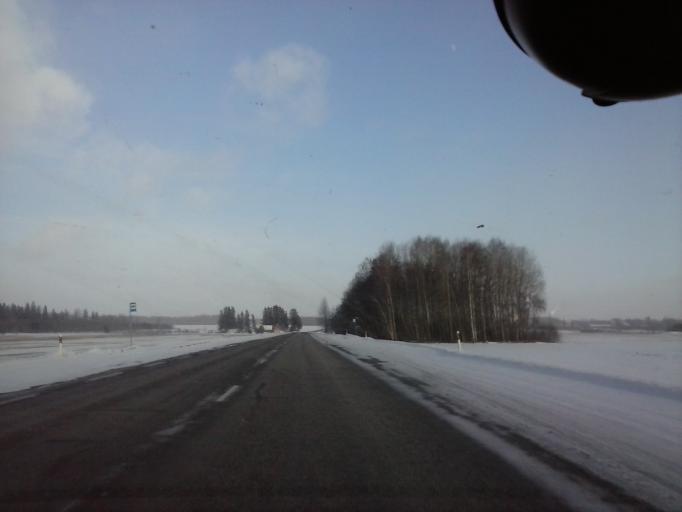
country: EE
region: Tartu
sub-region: Puhja vald
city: Puhja
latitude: 58.3273
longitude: 26.2708
